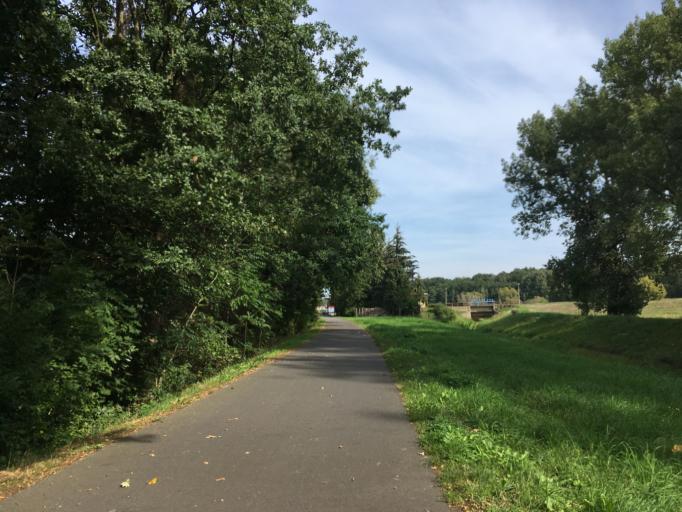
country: DE
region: Brandenburg
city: Forst
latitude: 51.8037
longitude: 14.6028
